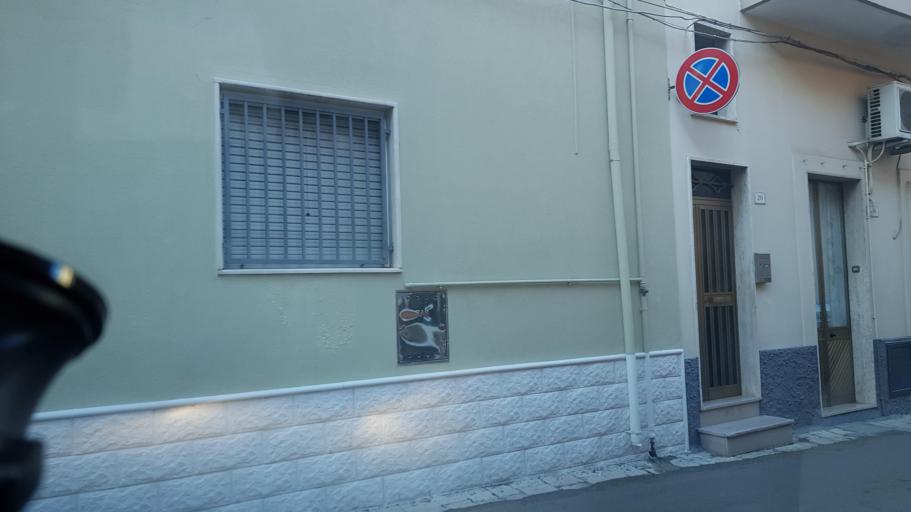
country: IT
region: Apulia
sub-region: Provincia di Brindisi
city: Latiano
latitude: 40.5531
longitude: 17.7166
